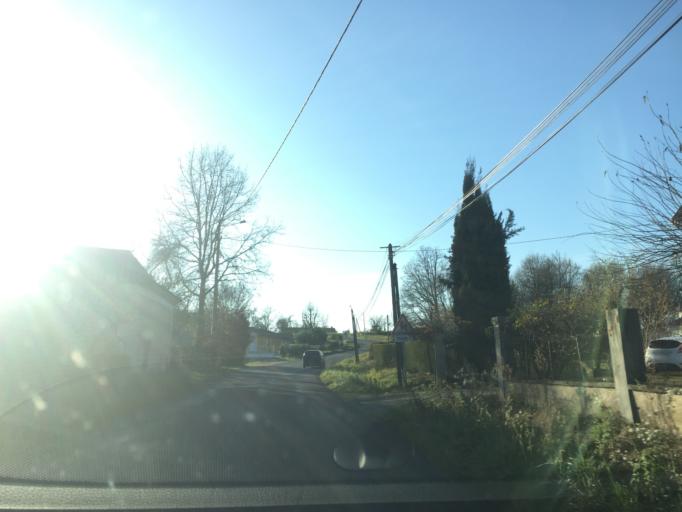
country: FR
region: Aquitaine
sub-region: Departement de la Dordogne
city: Saint-Astier
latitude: 45.1352
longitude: 0.5056
